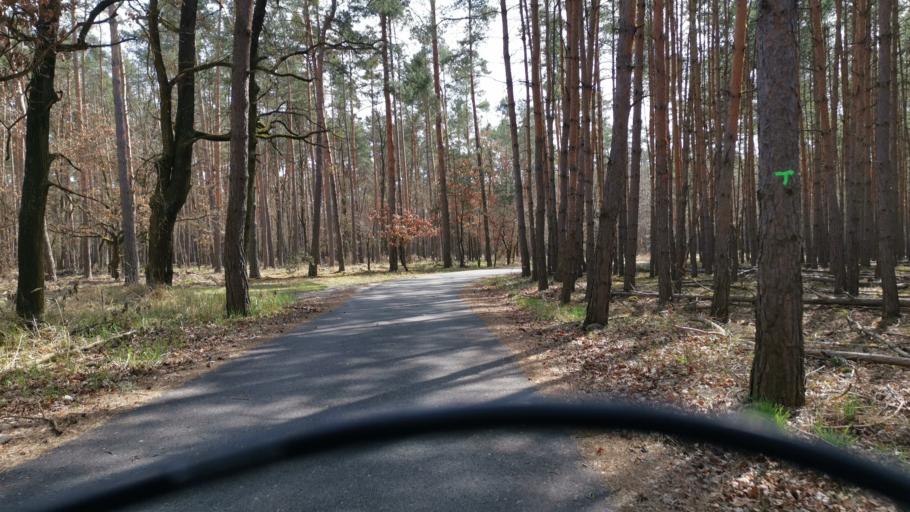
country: SK
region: Trnavsky
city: Gbely
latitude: 48.7177
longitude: 17.0524
